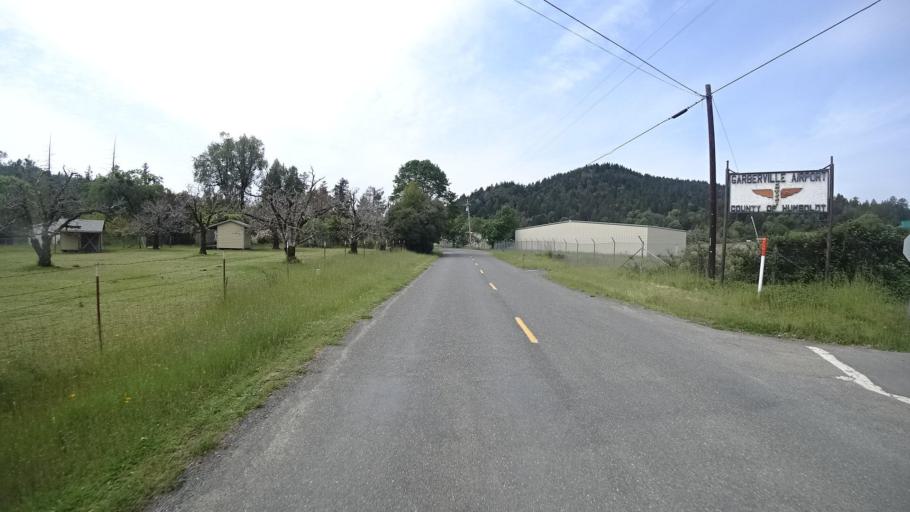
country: US
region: California
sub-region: Humboldt County
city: Redway
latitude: 40.0874
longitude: -123.8112
